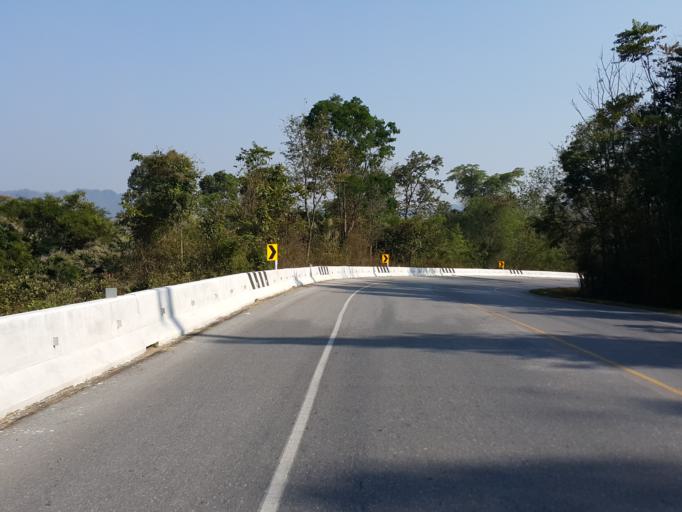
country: TH
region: Lampang
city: Chae Hom
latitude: 18.5967
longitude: 99.5484
